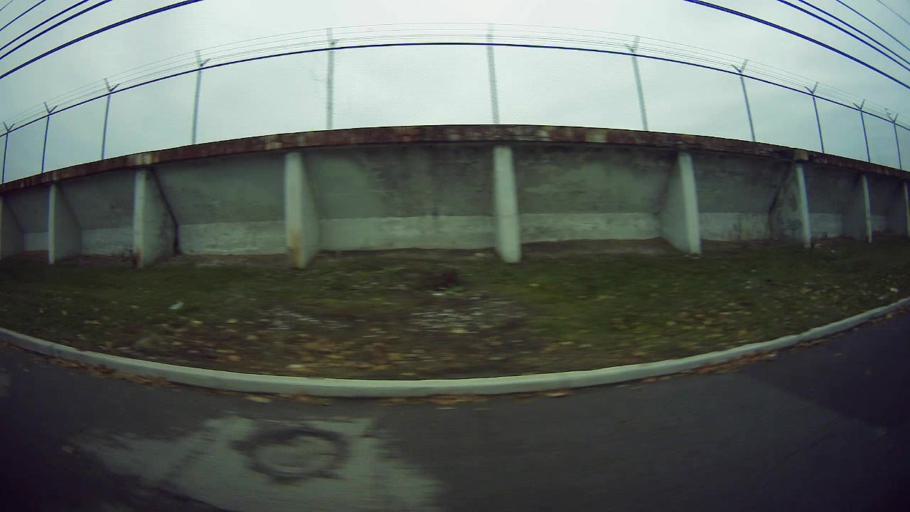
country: US
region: Michigan
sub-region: Wayne County
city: Highland Park
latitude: 42.4125
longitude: -83.0795
